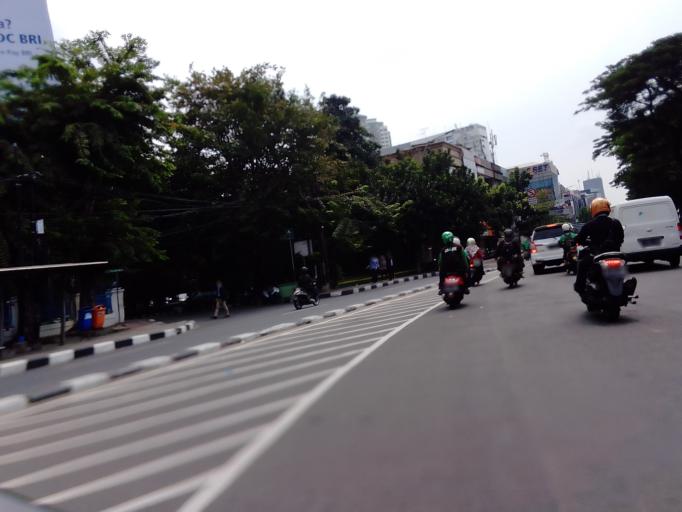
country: ID
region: Jakarta Raya
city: Jakarta
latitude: -6.1710
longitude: 106.8215
